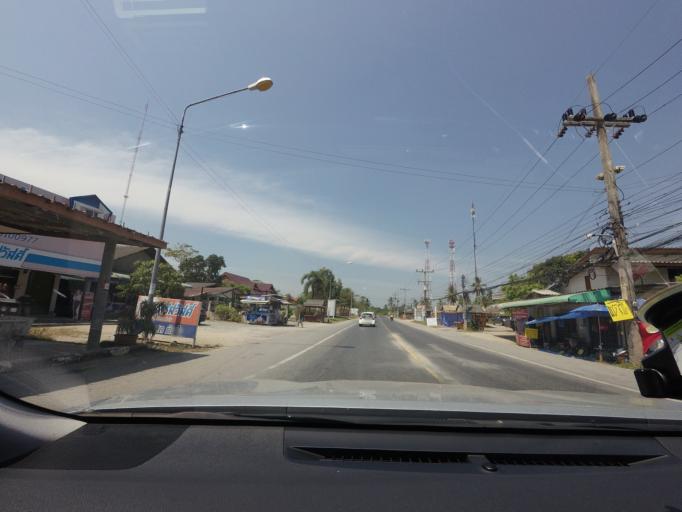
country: TH
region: Surat Thani
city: Phunphin
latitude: 9.1916
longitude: 99.2530
